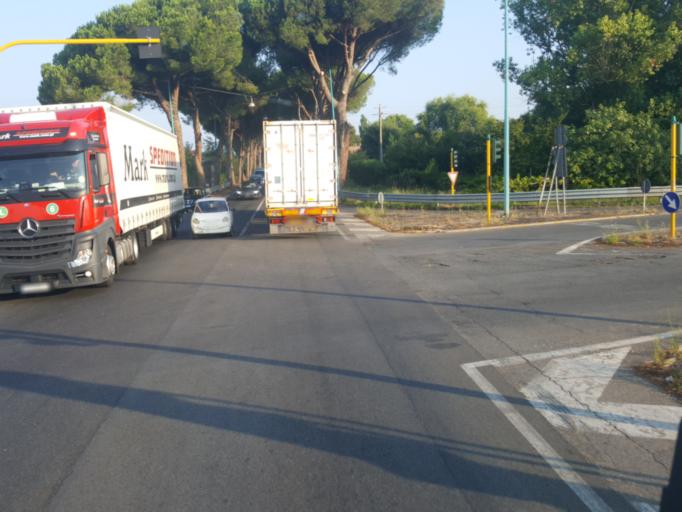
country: IT
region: Latium
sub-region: Provincia di Latina
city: Latina Scalo
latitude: 41.5149
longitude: 12.9358
